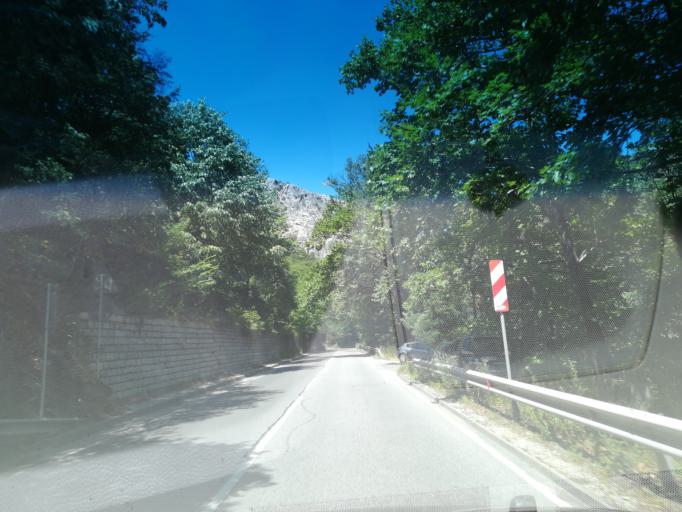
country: BG
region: Plovdiv
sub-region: Obshtina Asenovgrad
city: Asenovgrad
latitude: 41.9832
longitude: 24.8753
